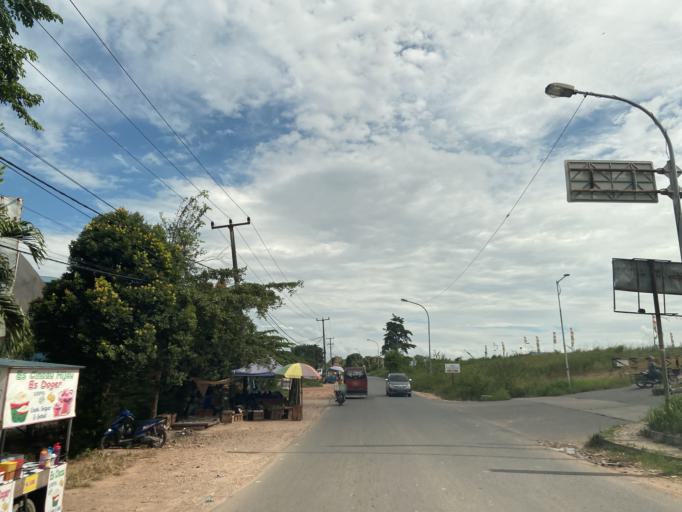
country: SG
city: Singapore
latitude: 1.0456
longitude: 103.9381
